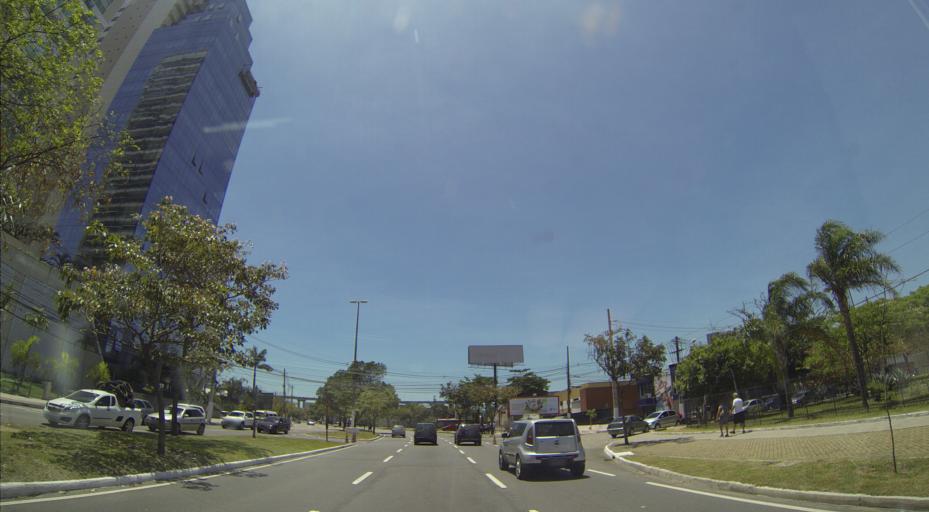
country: BR
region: Espirito Santo
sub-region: Vila Velha
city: Vila Velha
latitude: -20.3161
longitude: -40.2940
